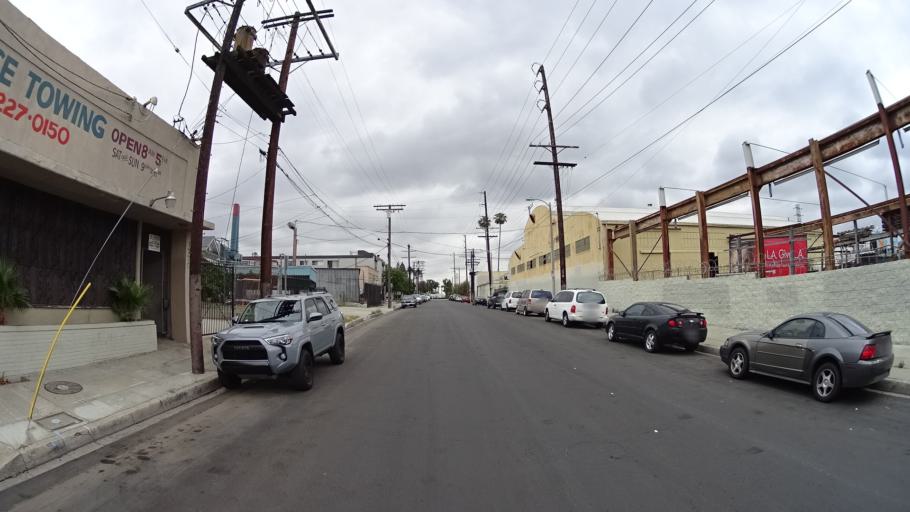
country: US
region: California
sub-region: Los Angeles County
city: Boyle Heights
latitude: 34.0631
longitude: -118.2140
